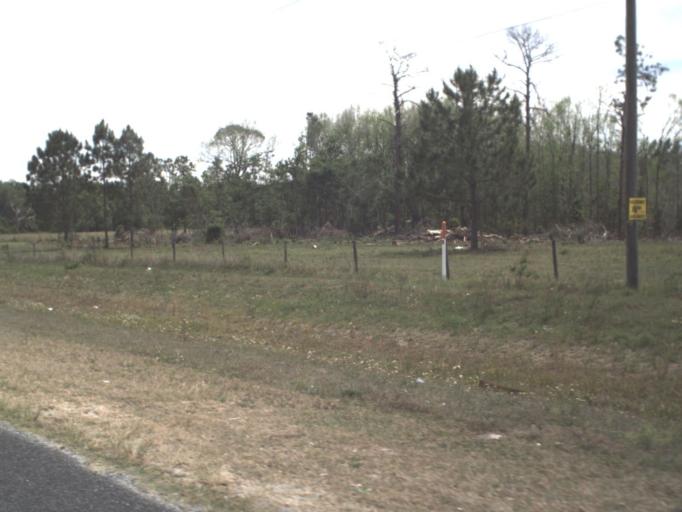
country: US
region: Florida
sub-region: Lake County
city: Fruitland Park
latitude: 28.8239
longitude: -81.9733
